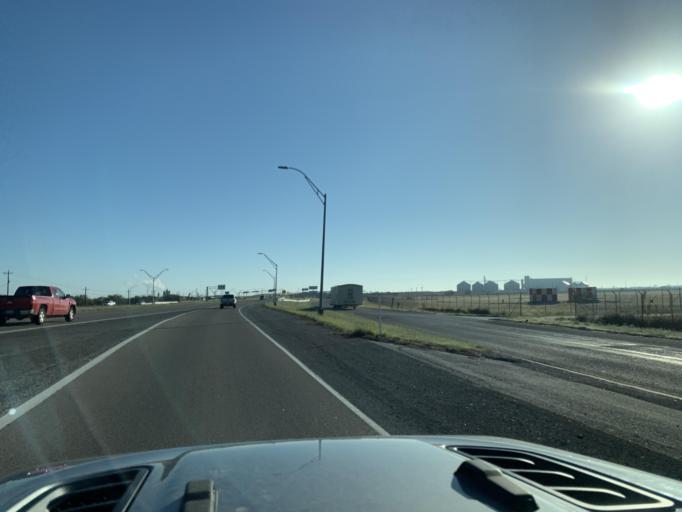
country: US
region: Texas
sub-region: Nueces County
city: Corpus Christi
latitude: 27.7847
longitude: -97.4988
